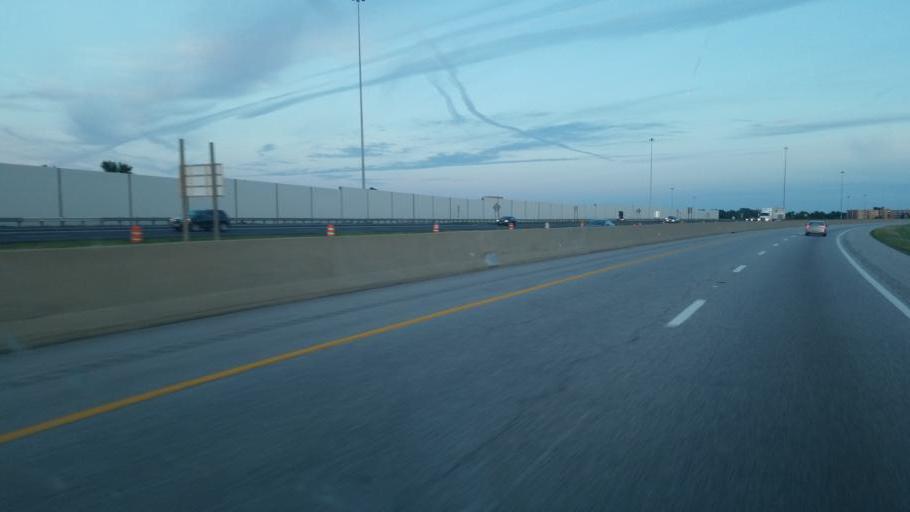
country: US
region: Ohio
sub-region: Cuyahoga County
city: Mayfield Heights
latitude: 41.5259
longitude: -81.4452
